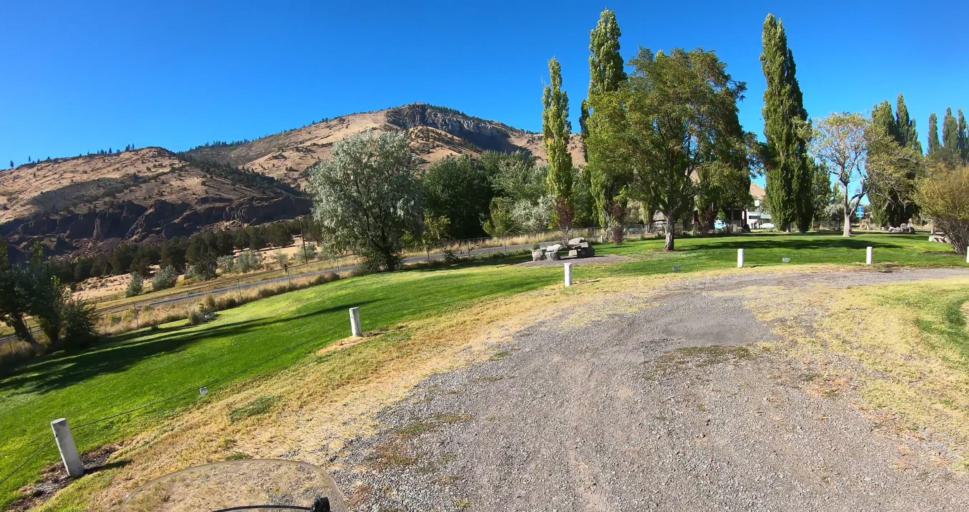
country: US
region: Oregon
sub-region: Lake County
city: Lakeview
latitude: 42.9714
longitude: -120.7781
